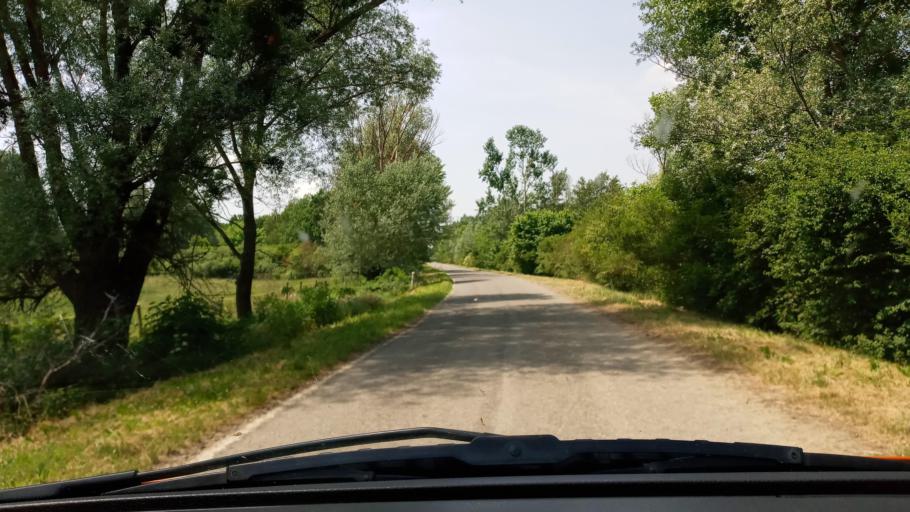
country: HU
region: Baranya
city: Sellye
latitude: 45.8092
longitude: 17.8683
